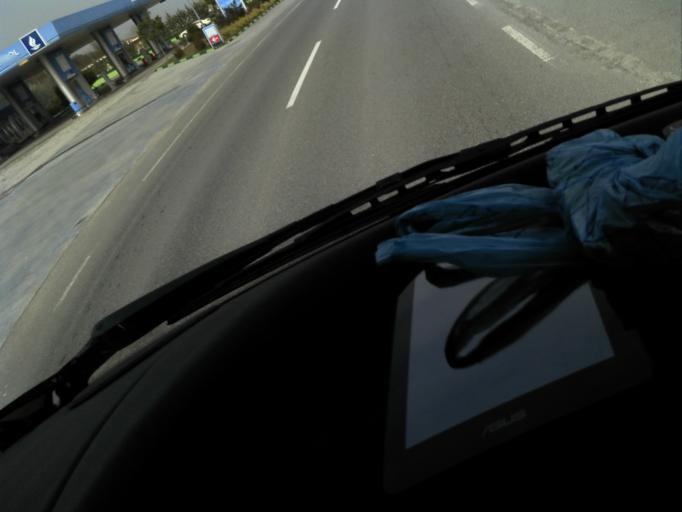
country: AL
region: Tirane
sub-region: Rrethi i Tiranes
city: Preze
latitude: 41.4134
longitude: 19.6855
